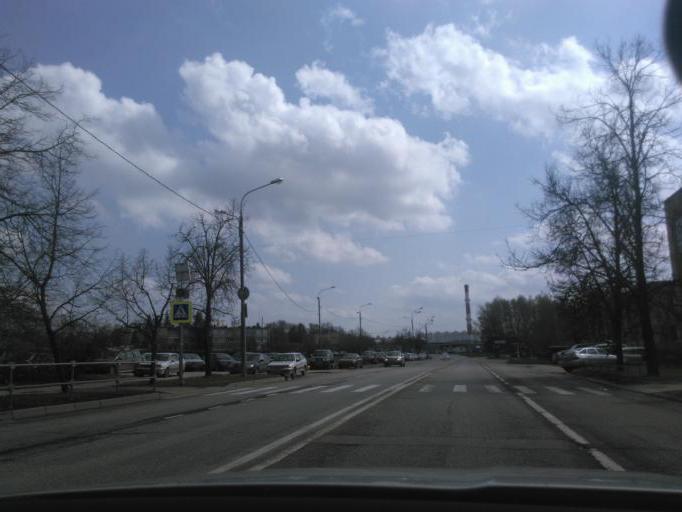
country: RU
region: Moscow
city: Zelenograd
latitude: 56.0121
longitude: 37.1915
